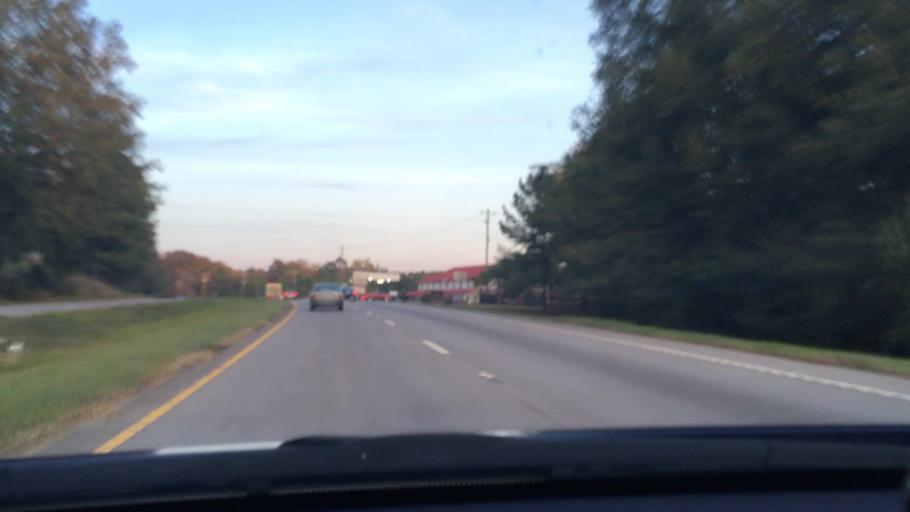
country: US
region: South Carolina
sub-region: Richland County
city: Hopkins
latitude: 33.9390
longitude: -80.7880
